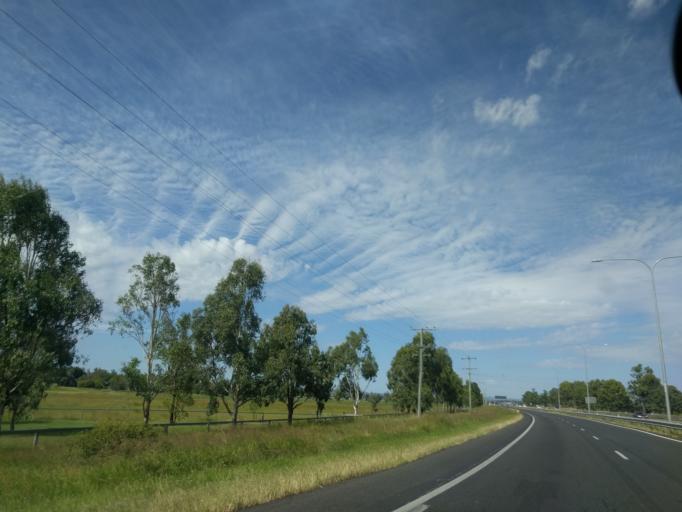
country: AU
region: Queensland
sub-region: Lockyer Valley
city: Gatton
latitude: -27.5455
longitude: 152.3399
